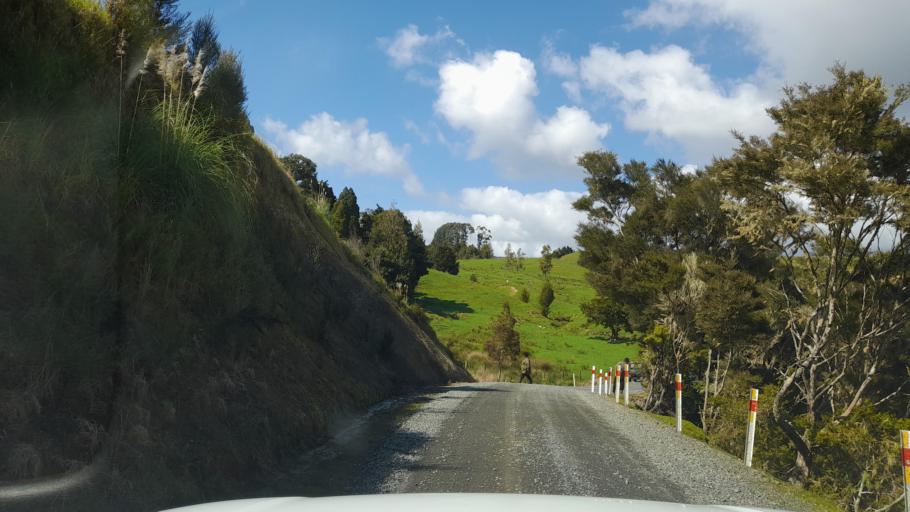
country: NZ
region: Northland
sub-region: Far North District
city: Waimate North
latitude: -35.1537
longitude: 173.7155
